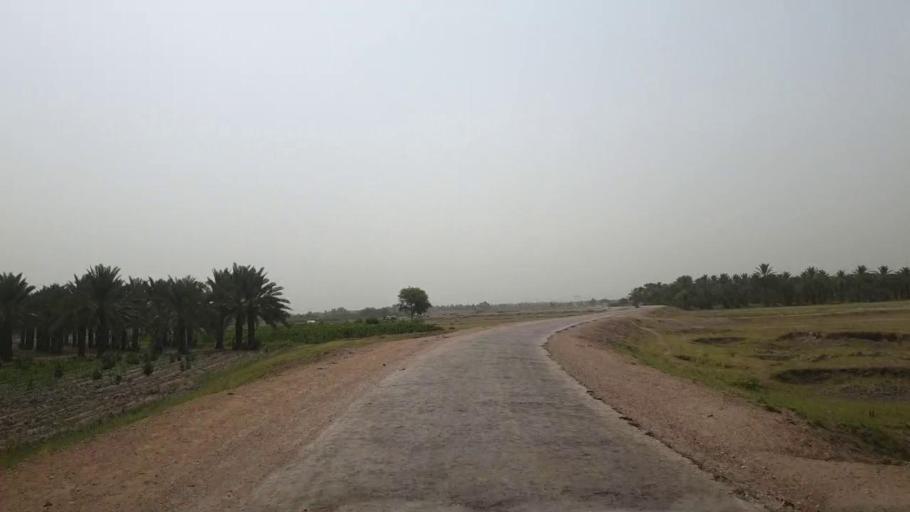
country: PK
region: Sindh
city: Gambat
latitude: 27.4258
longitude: 68.5409
